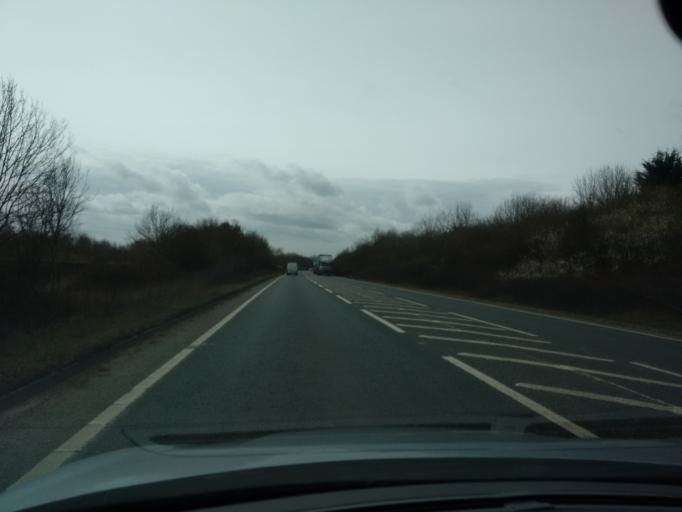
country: GB
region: England
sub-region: Worcestershire
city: Evesham
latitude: 52.0803
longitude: -1.9301
